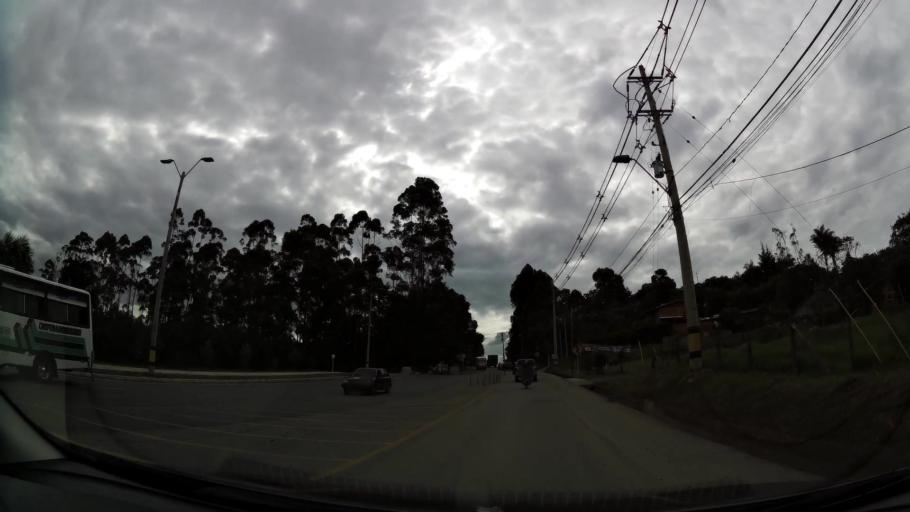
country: CO
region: Antioquia
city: Rionegro
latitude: 6.1526
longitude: -75.3995
